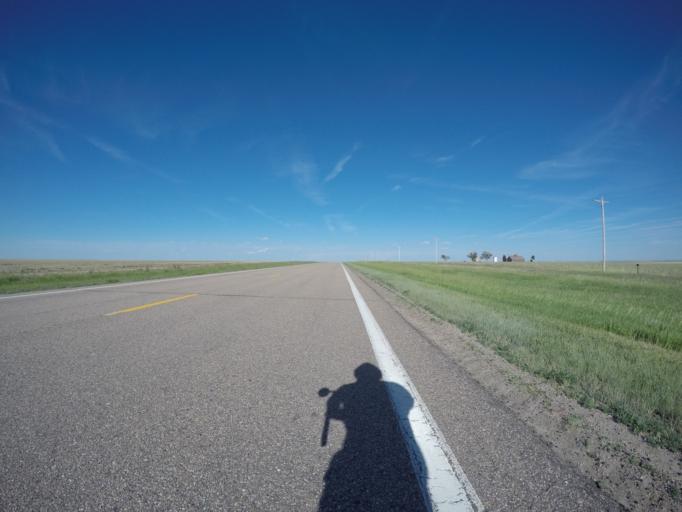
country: US
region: Kansas
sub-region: Cheyenne County
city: Saint Francis
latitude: 39.7565
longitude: -101.9893
